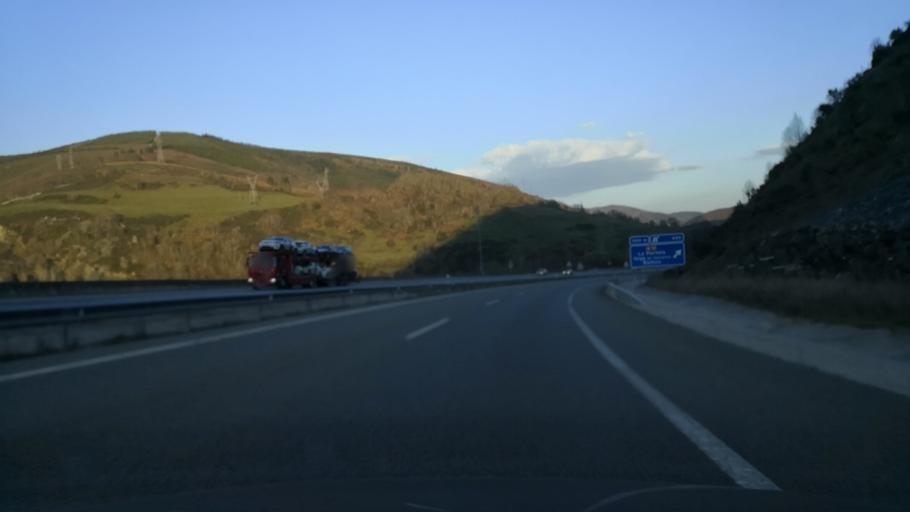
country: ES
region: Castille and Leon
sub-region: Provincia de Leon
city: Vega de Valcarce
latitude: 42.6643
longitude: -6.9328
